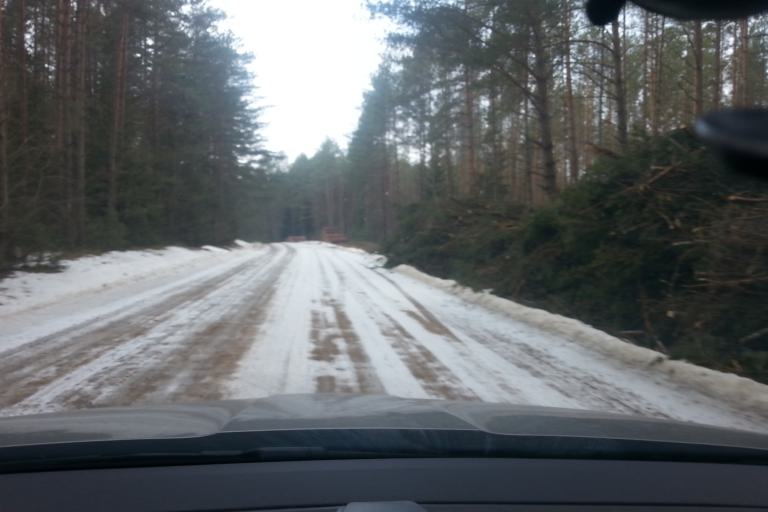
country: LT
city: Trakai
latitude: 54.5283
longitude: 24.9695
